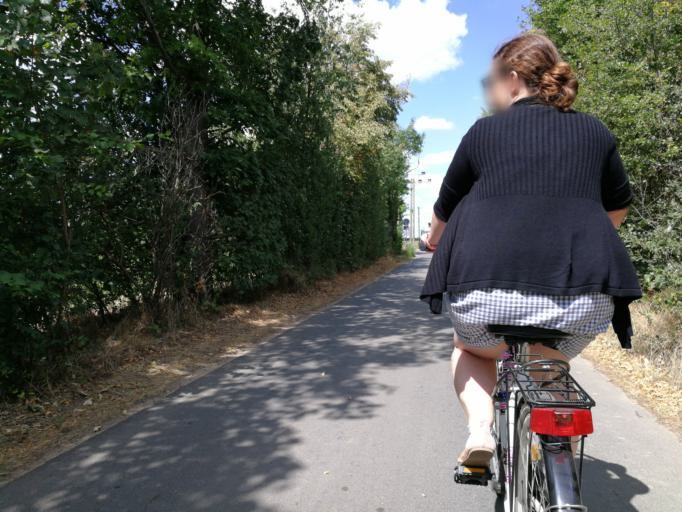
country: DE
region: North Rhine-Westphalia
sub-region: Regierungsbezirk Dusseldorf
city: Dormagen
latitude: 51.0947
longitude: 6.7769
